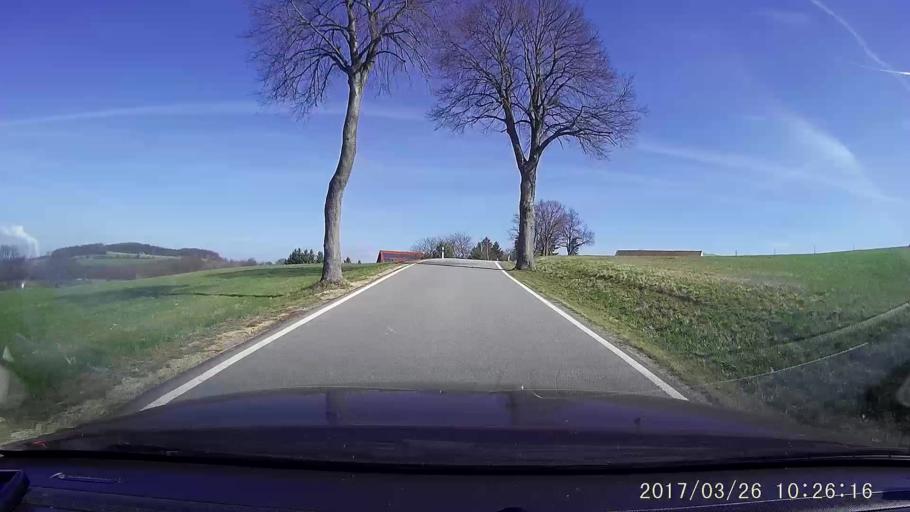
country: DE
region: Saxony
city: Sohland am Rotstein
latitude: 51.1132
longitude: 14.7364
